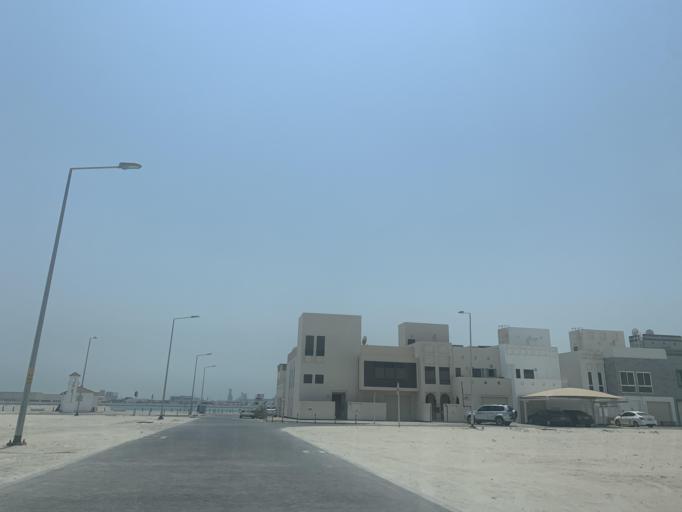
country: BH
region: Muharraq
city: Al Hadd
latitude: 26.2340
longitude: 50.6780
